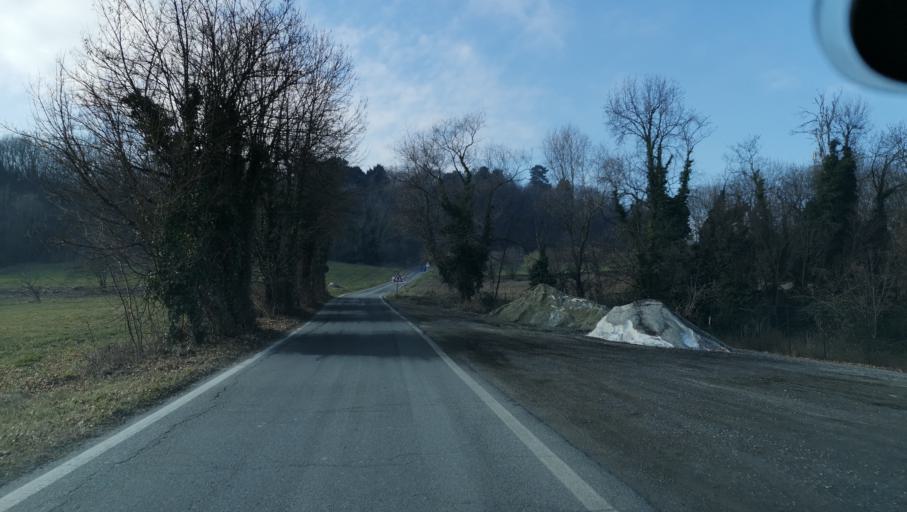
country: IT
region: Piedmont
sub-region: Provincia di Torino
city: Sciolze
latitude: 45.0956
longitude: 7.8738
